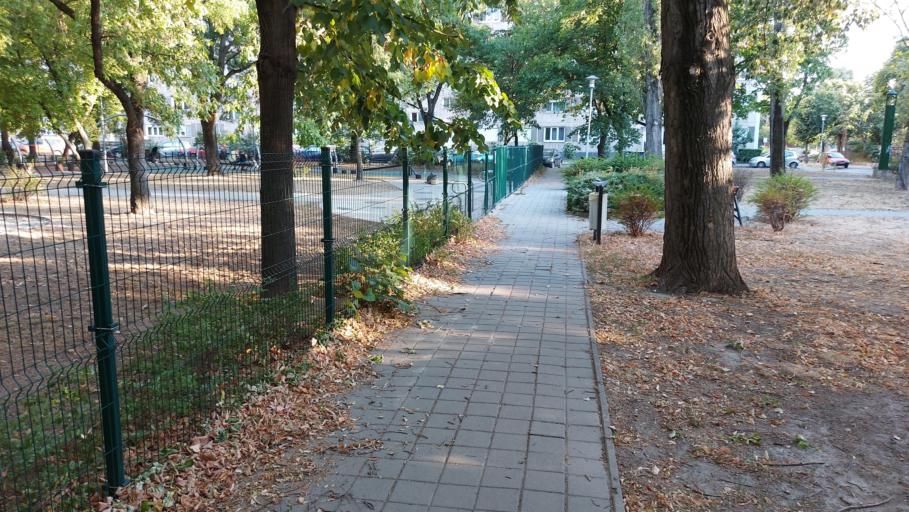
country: HU
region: Budapest
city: Budapest XI. keruelet
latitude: 47.4572
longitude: 19.0369
